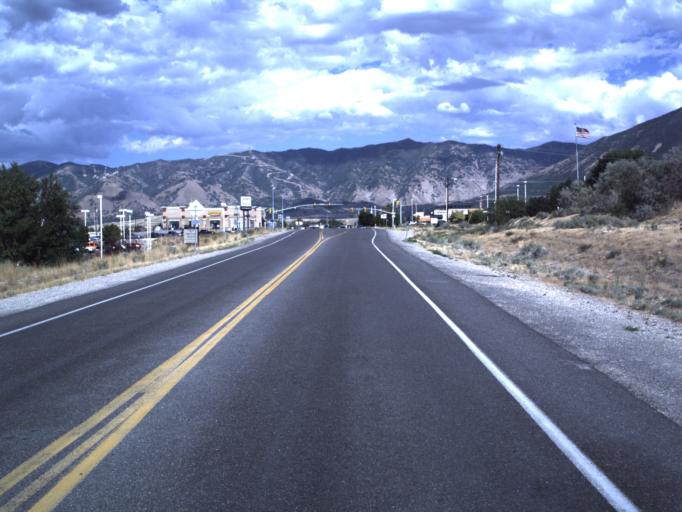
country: US
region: Utah
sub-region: Tooele County
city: Tooele
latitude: 40.5510
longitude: -112.3013
